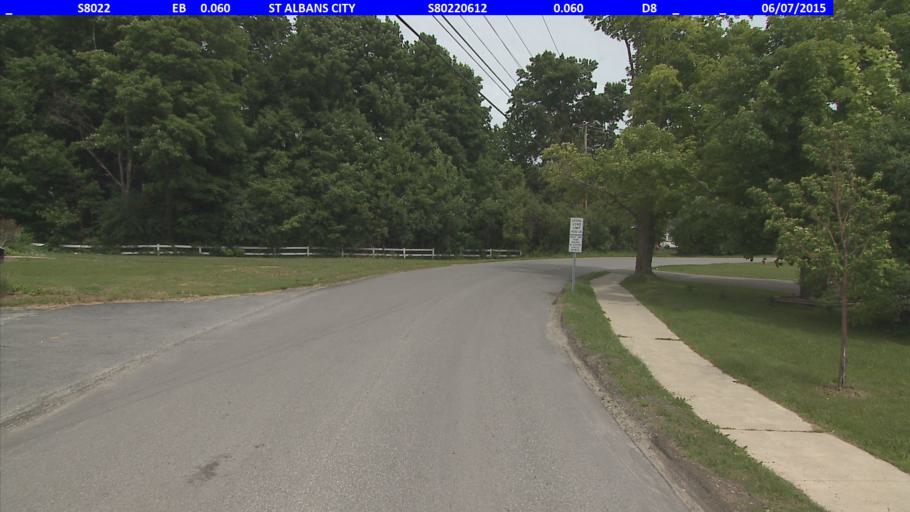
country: US
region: Vermont
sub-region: Franklin County
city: Saint Albans
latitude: 44.8043
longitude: -73.0950
